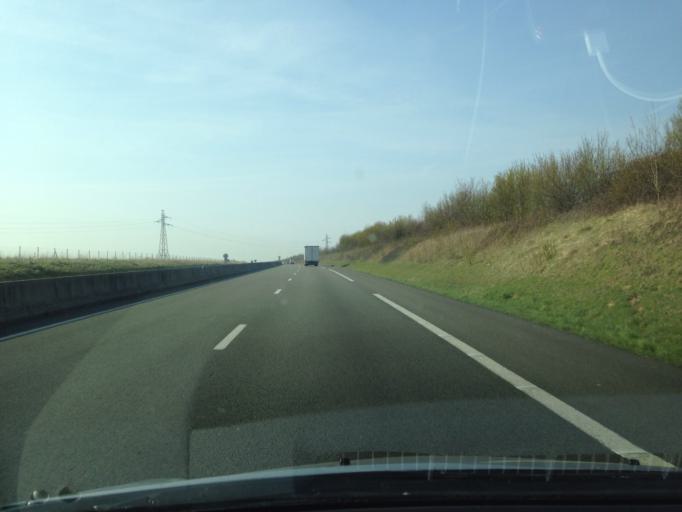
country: FR
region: Picardie
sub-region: Departement de la Somme
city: Sailly-Flibeaucourt
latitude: 50.1504
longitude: 1.7966
